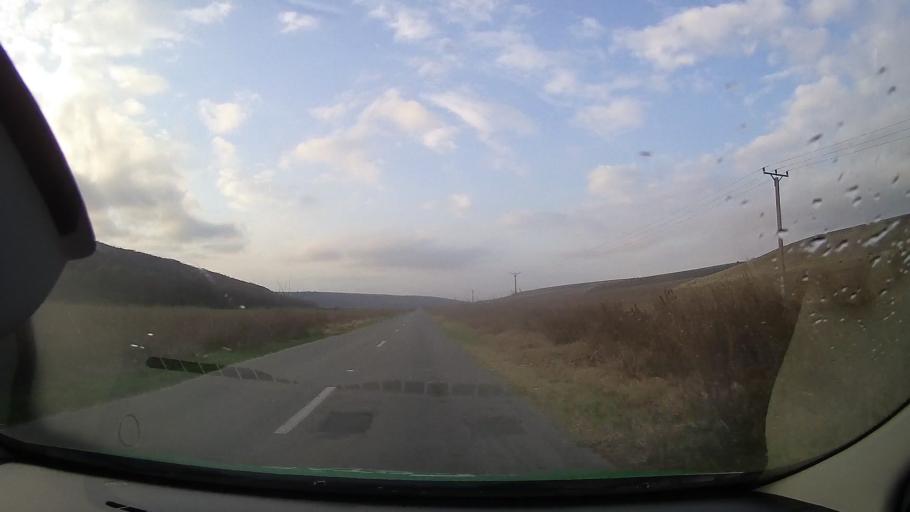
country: RO
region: Constanta
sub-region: Comuna Dobromir
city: Dobromir
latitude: 44.0296
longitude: 27.8607
